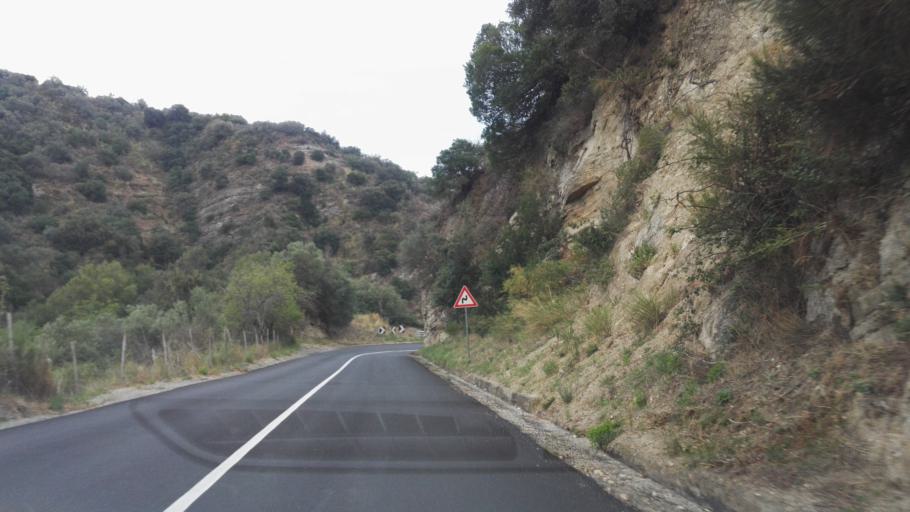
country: IT
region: Calabria
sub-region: Provincia di Reggio Calabria
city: Caulonia
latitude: 38.4002
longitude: 16.4133
